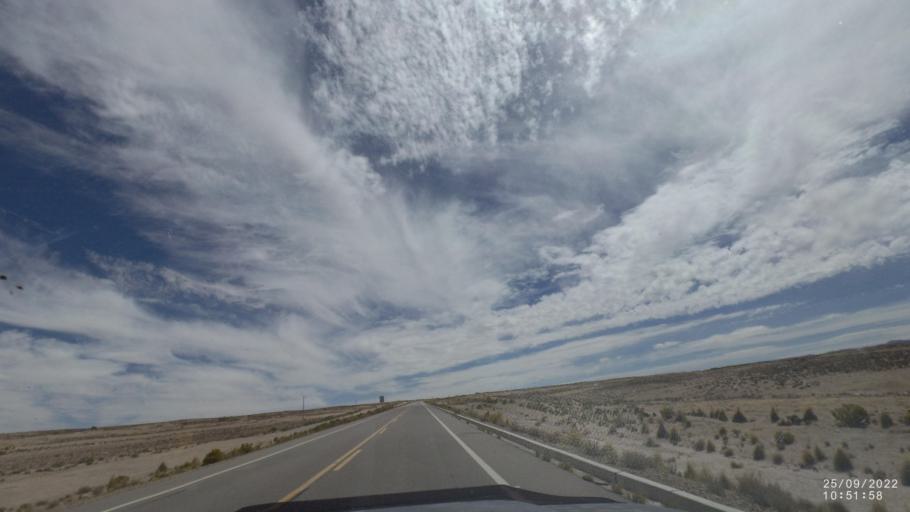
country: BO
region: Oruro
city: Challapata
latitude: -19.5553
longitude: -66.8528
